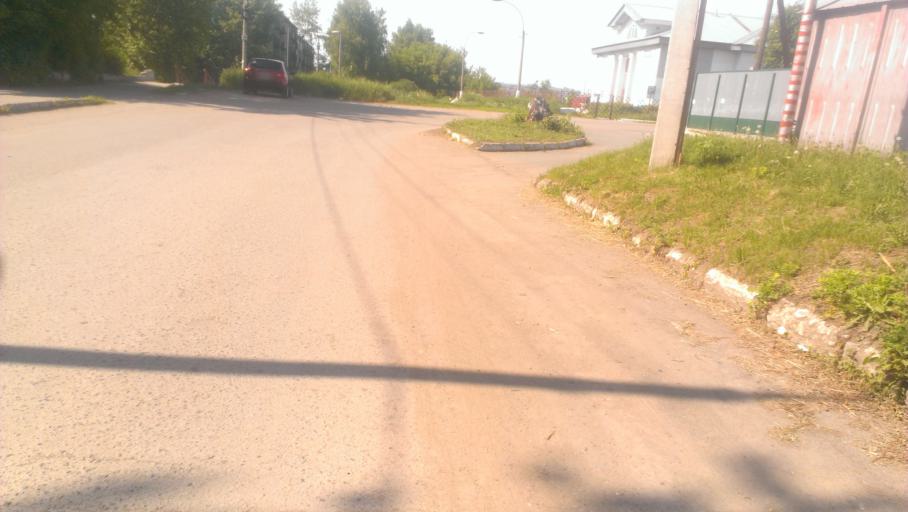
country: RU
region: Altai Krai
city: Novoaltaysk
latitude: 53.3970
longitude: 83.9355
